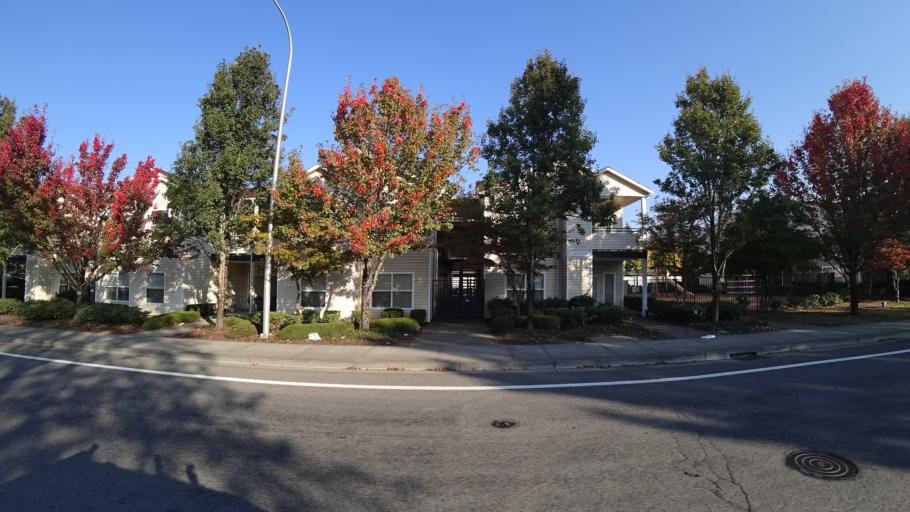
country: US
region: Oregon
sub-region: Multnomah County
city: Fairview
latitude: 45.5177
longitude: -122.4552
